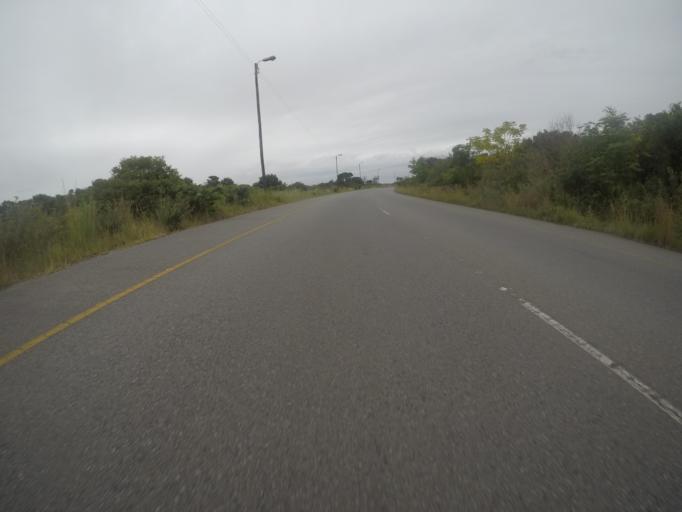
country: ZA
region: Eastern Cape
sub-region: Buffalo City Metropolitan Municipality
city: East London
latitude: -32.9672
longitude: 27.8585
